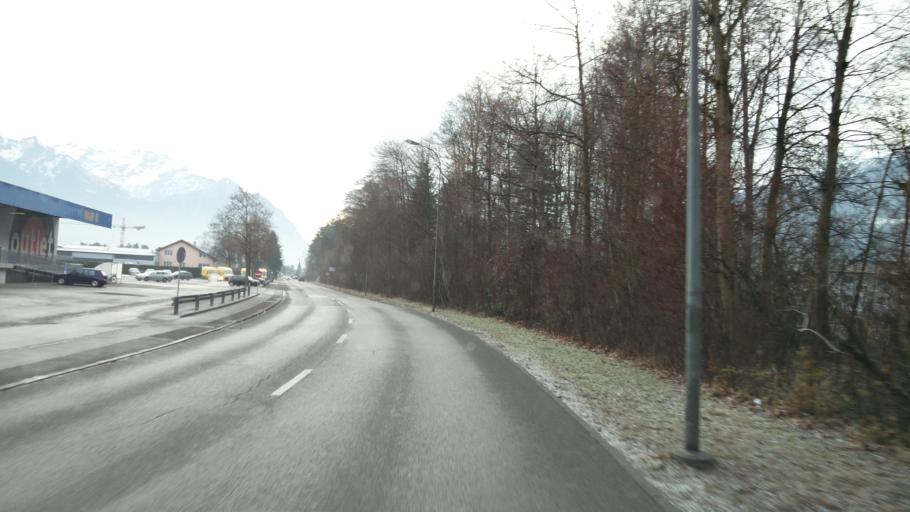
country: CH
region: Saint Gallen
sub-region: Wahlkreis Werdenberg
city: Buchs
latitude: 47.1639
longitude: 9.4778
